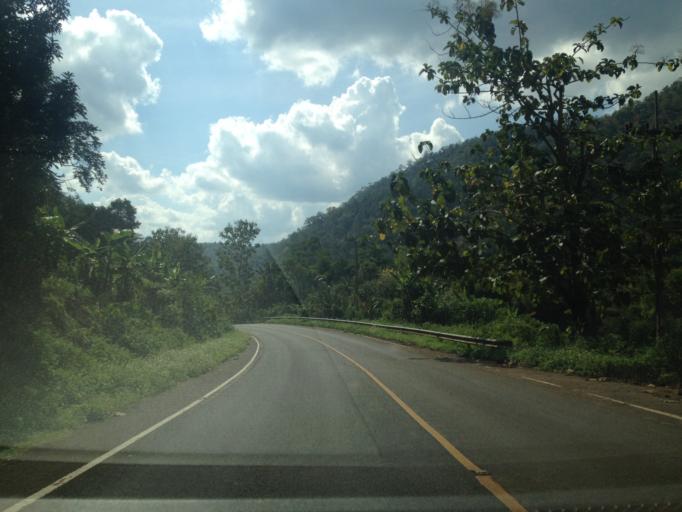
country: TH
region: Chiang Mai
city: Samoeng
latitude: 18.8020
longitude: 98.7960
